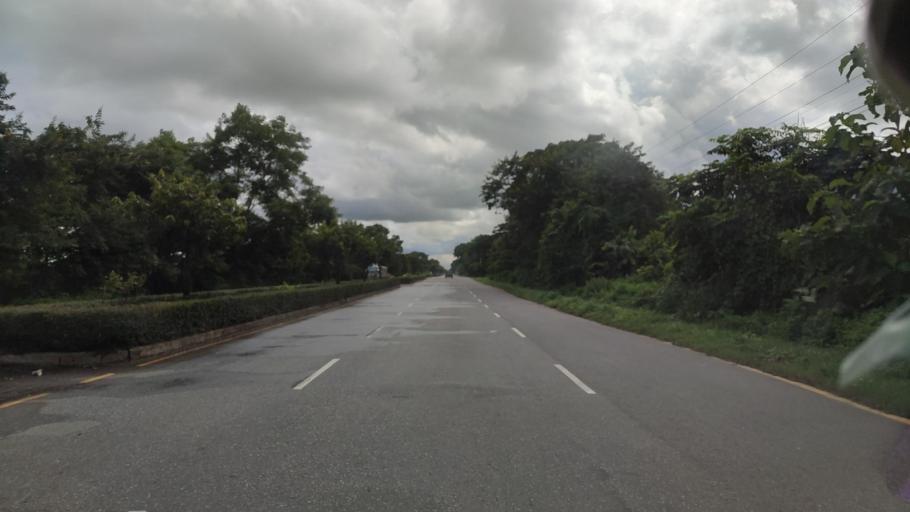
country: MM
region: Bago
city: Thanatpin
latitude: 17.1256
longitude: 96.2679
